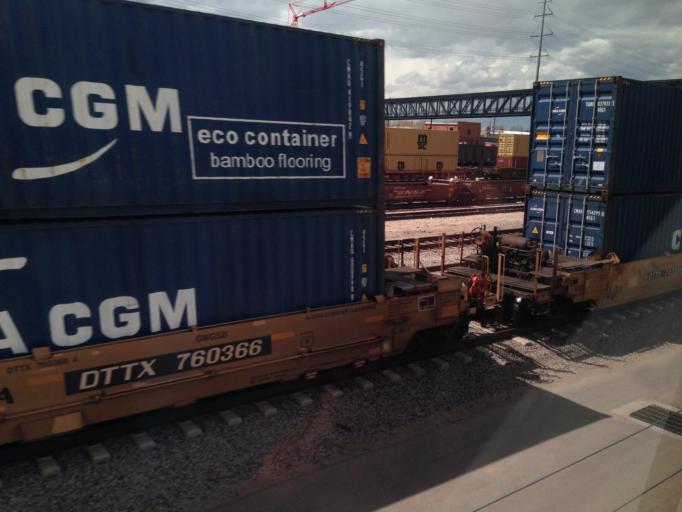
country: US
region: Colorado
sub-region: Denver County
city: Denver
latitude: 39.7721
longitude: -104.9971
